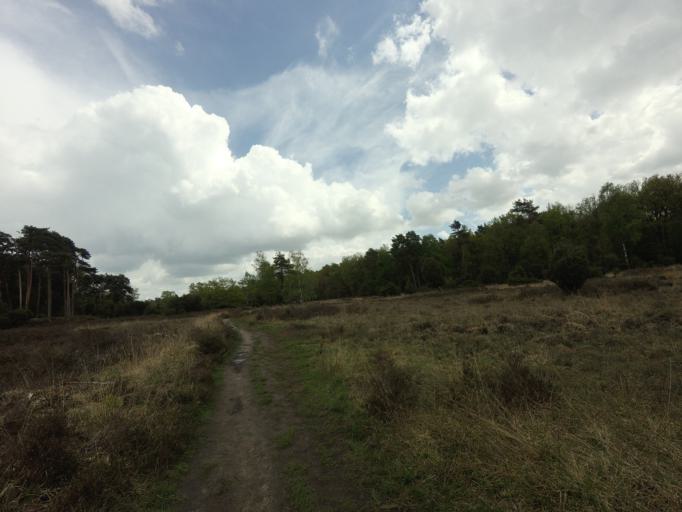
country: NL
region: Overijssel
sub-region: Gemeente Haaksbergen
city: Haaksbergen
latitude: 52.1529
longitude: 6.8038
